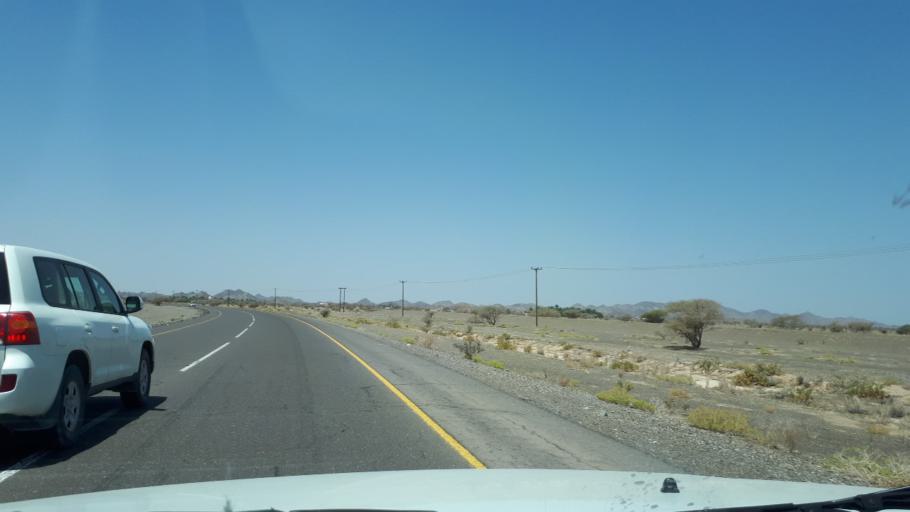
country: OM
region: Ash Sharqiyah
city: Ibra'
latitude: 22.6205
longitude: 58.4078
